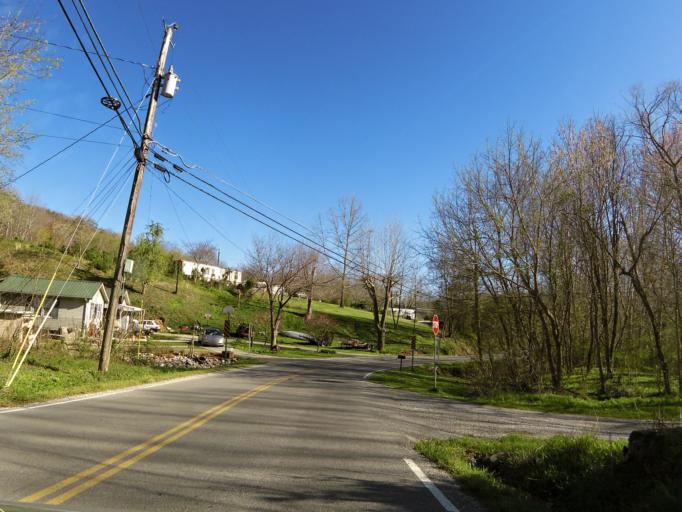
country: US
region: Tennessee
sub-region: Scott County
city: Huntsville
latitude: 36.3401
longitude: -84.3861
